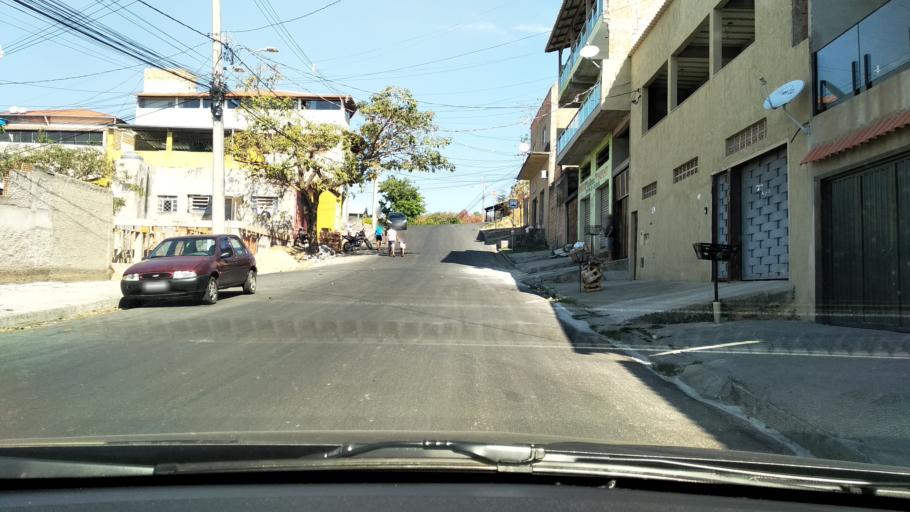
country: BR
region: Minas Gerais
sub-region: Belo Horizonte
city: Belo Horizonte
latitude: -19.8597
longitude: -43.8760
